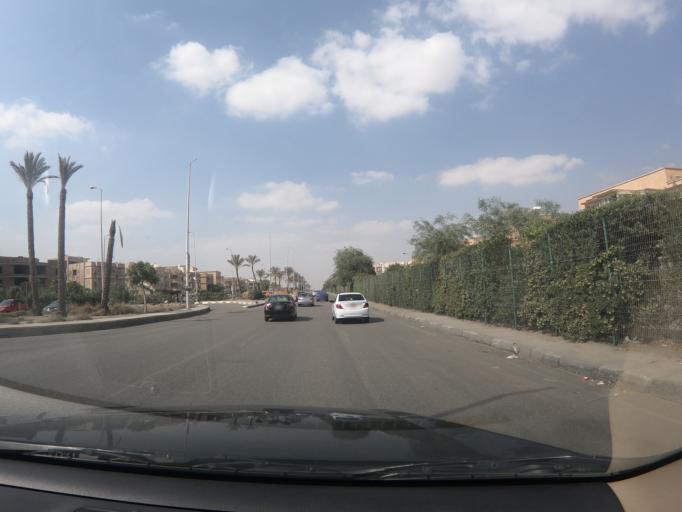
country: EG
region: Muhafazat al Qalyubiyah
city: Al Khankah
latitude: 30.0590
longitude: 31.4751
